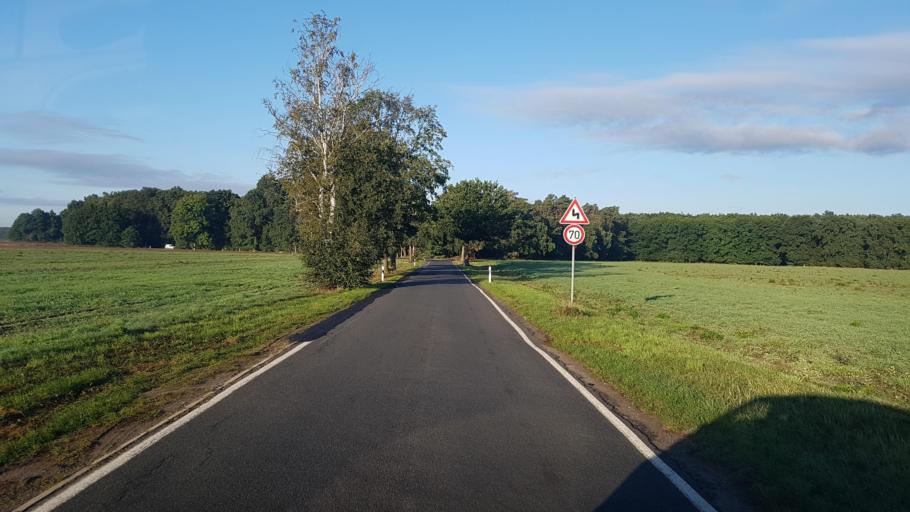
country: DE
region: Saxony-Anhalt
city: Holzdorf
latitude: 51.8257
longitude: 13.1079
